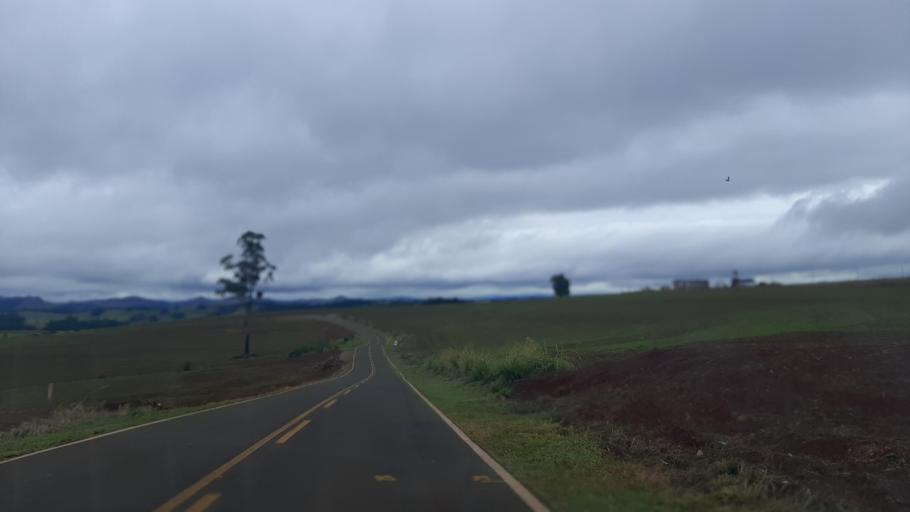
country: BR
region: Parana
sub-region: Ampere
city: Ampere
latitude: -25.9514
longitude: -53.4581
